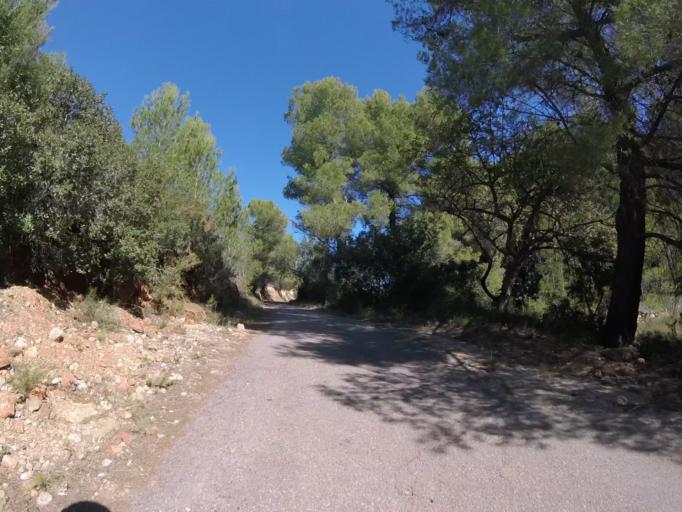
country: ES
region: Valencia
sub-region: Provincia de Castello
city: Cabanes
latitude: 40.1418
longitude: 0.1025
